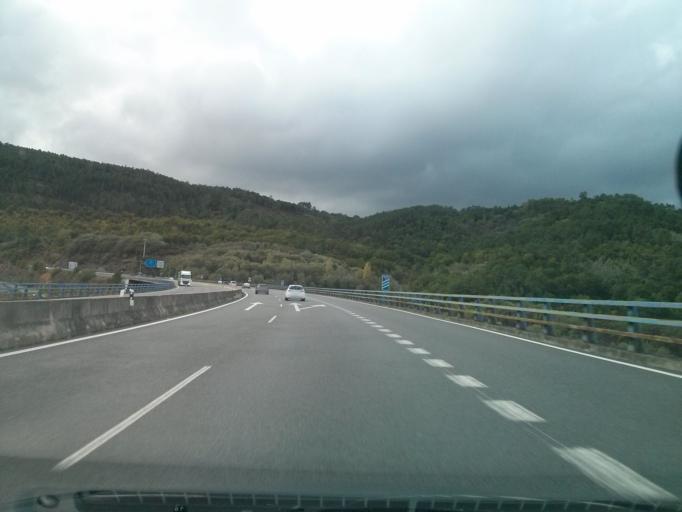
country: ES
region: Galicia
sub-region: Provincia de Ourense
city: Punxin
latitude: 42.3433
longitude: -8.0047
